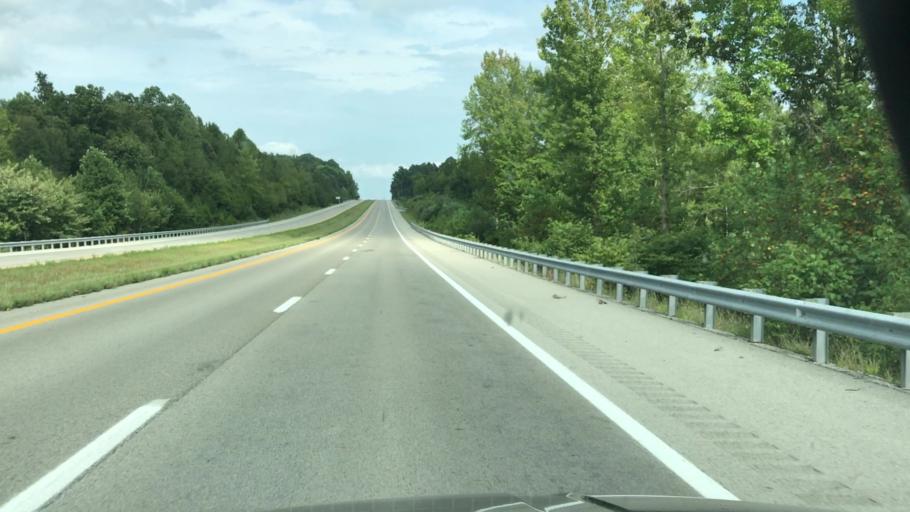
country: US
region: Kentucky
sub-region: Hopkins County
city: Earlington
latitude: 37.1996
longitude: -87.5440
